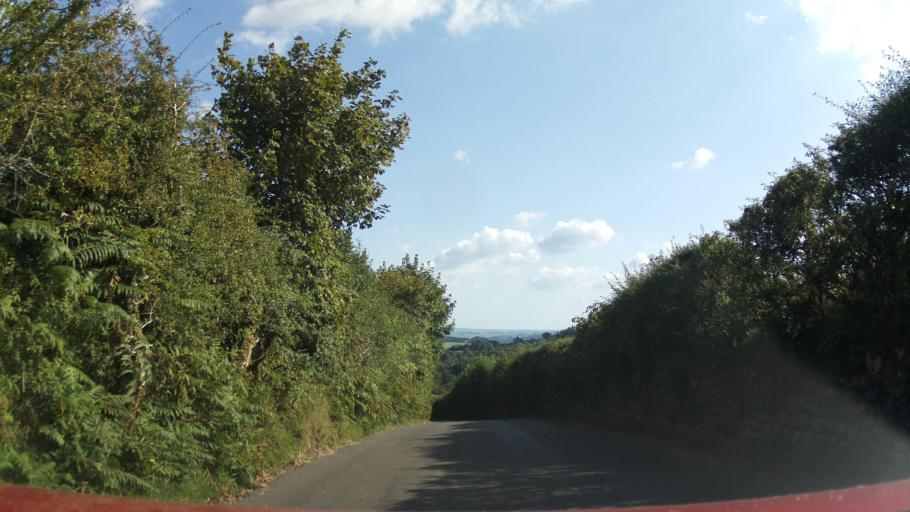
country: GB
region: England
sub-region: Devon
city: Buckfastleigh
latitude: 50.5427
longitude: -3.8350
